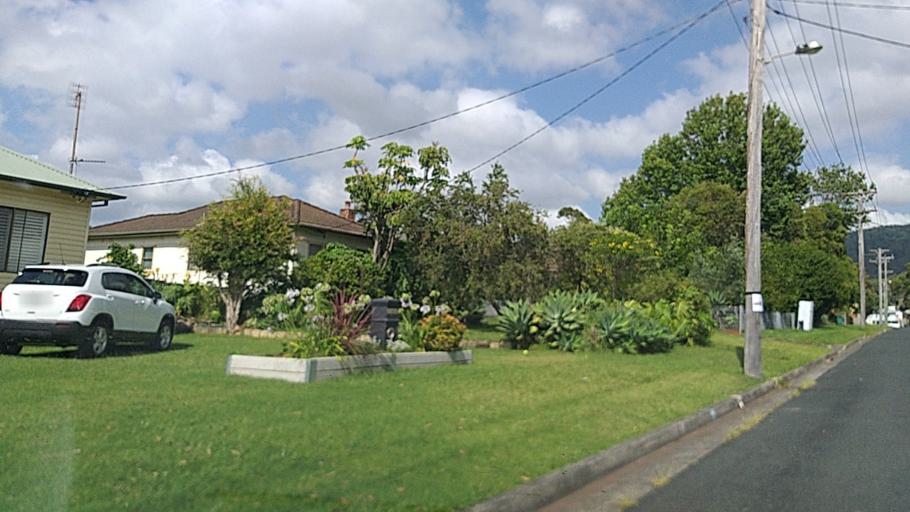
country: AU
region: New South Wales
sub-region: Wollongong
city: Corrimal
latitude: -34.3793
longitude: 150.8927
